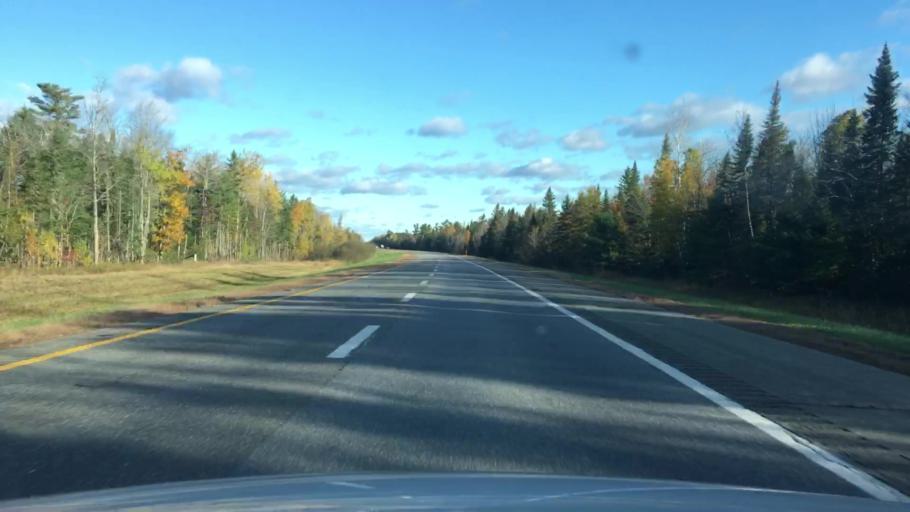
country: US
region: Maine
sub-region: Penobscot County
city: Greenbush
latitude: 45.0528
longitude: -68.6873
